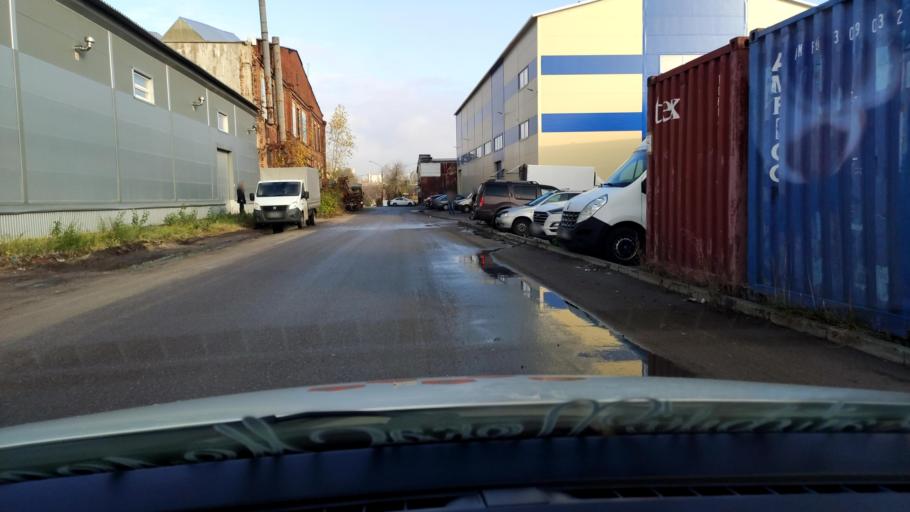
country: RU
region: Voronezj
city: Voronezh
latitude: 51.6892
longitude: 39.1752
